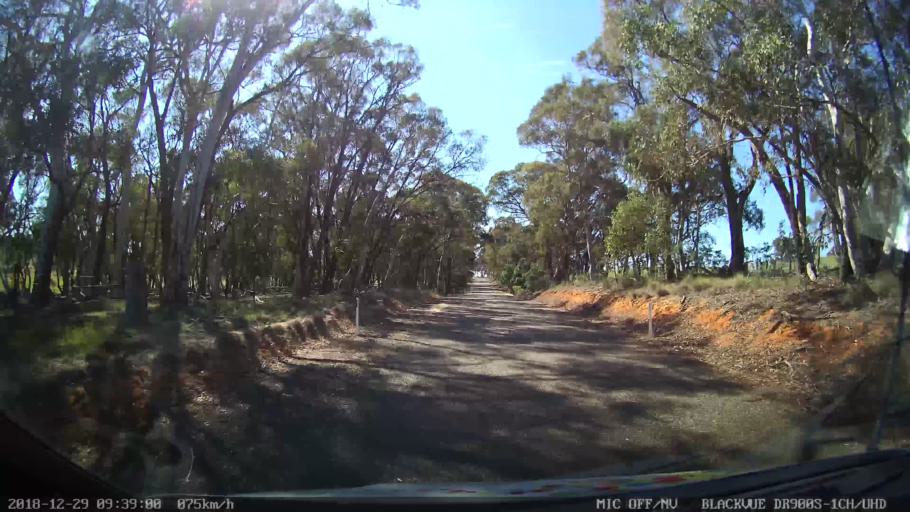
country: AU
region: New South Wales
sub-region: Upper Lachlan Shire
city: Crookwell
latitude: -34.6513
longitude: 149.3808
